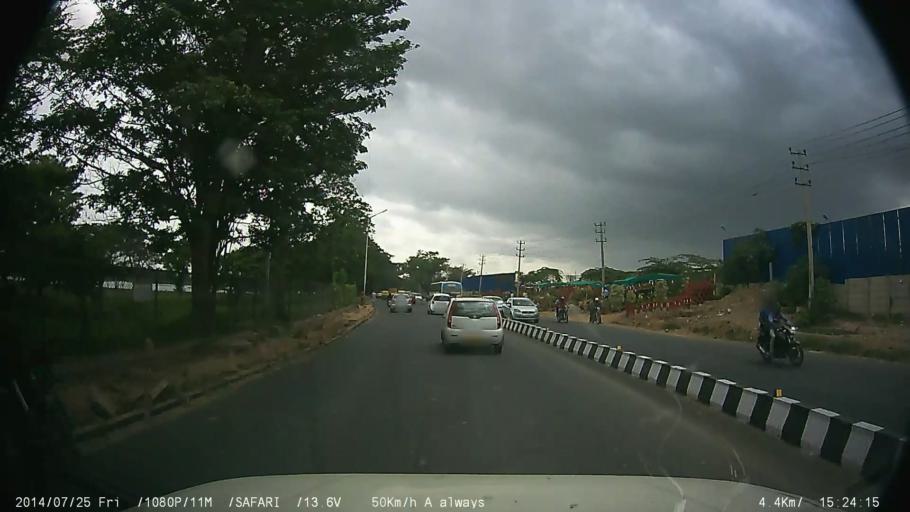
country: IN
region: Karnataka
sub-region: Bangalore Urban
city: Bangalore
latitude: 12.9245
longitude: 77.6453
